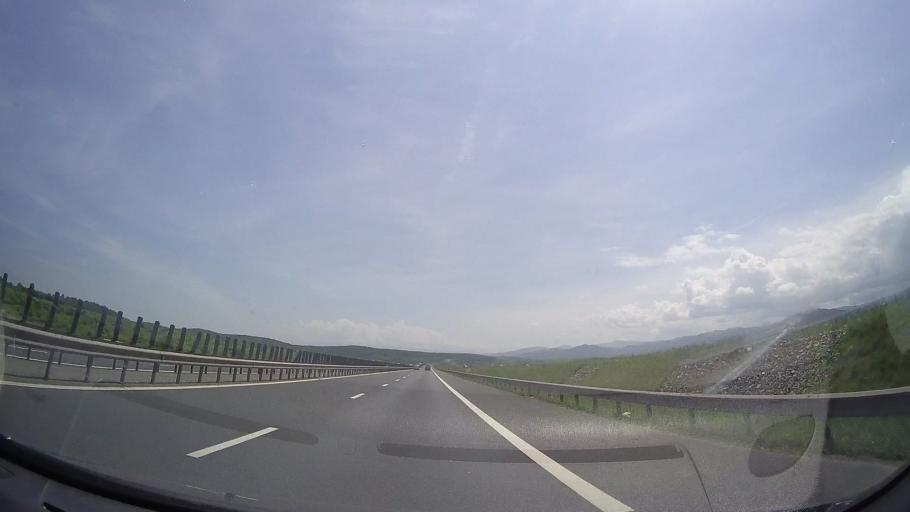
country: RO
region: Sibiu
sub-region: Oras Saliste
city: Saliste
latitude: 45.8009
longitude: 23.9232
